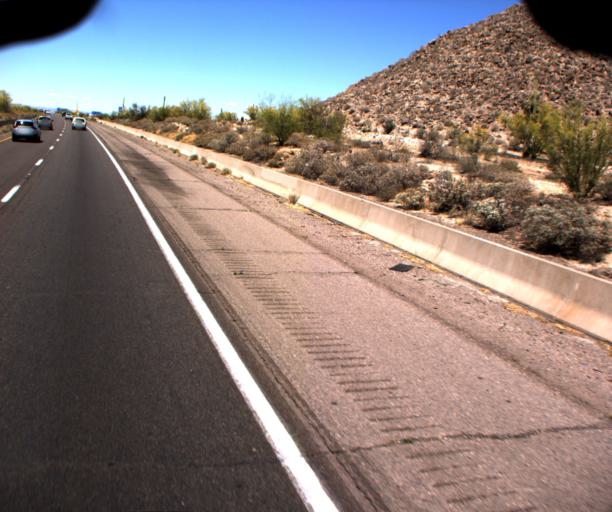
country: US
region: Arizona
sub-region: Pinal County
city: Sacaton
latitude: 33.0221
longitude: -111.7674
